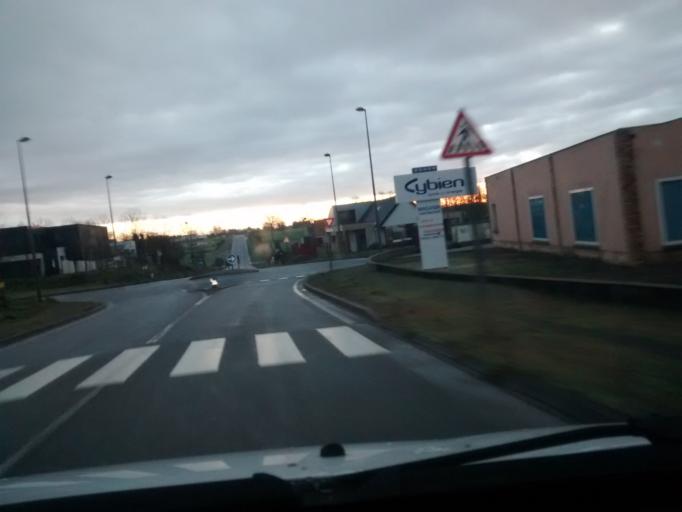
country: FR
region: Brittany
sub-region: Departement d'Ille-et-Vilaine
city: Chateaubourg
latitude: 48.1004
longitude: -1.4110
